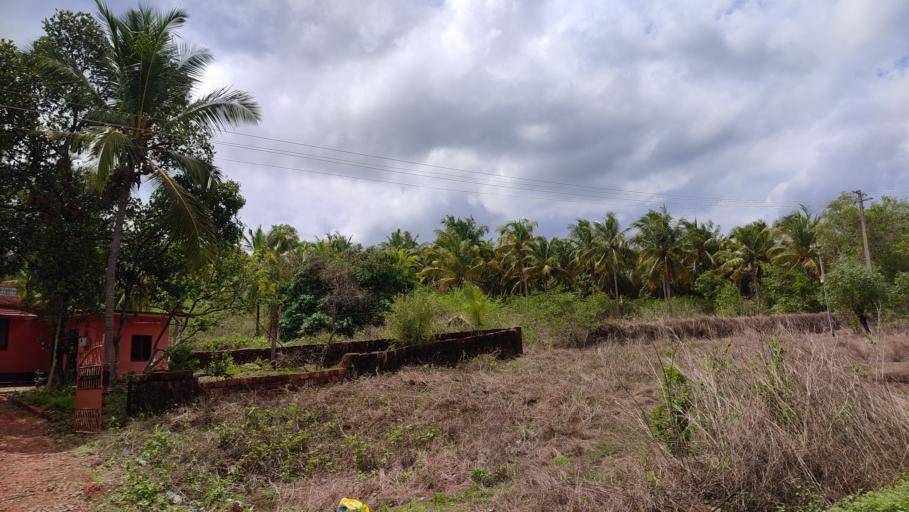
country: IN
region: Kerala
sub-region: Kasaragod District
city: Kannangad
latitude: 12.3873
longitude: 75.1010
